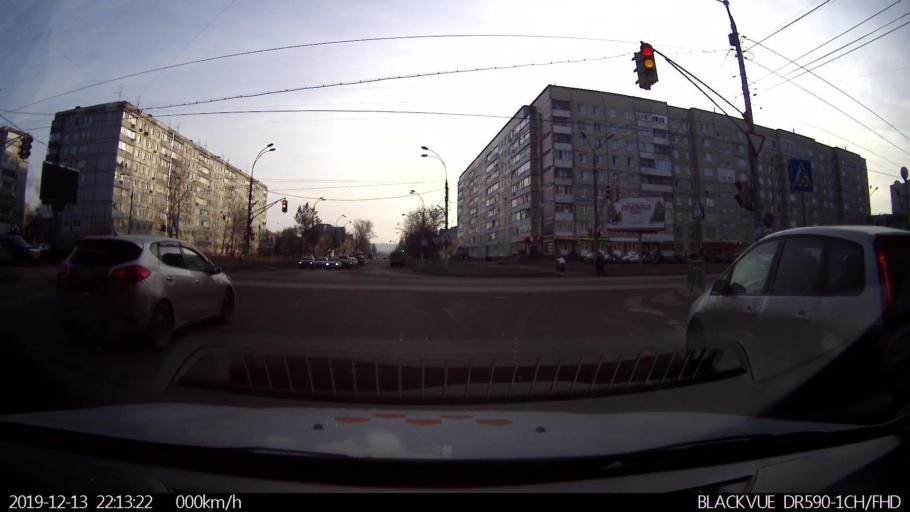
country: RU
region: Nizjnij Novgorod
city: Nizhniy Novgorod
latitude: 56.2708
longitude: 43.8865
